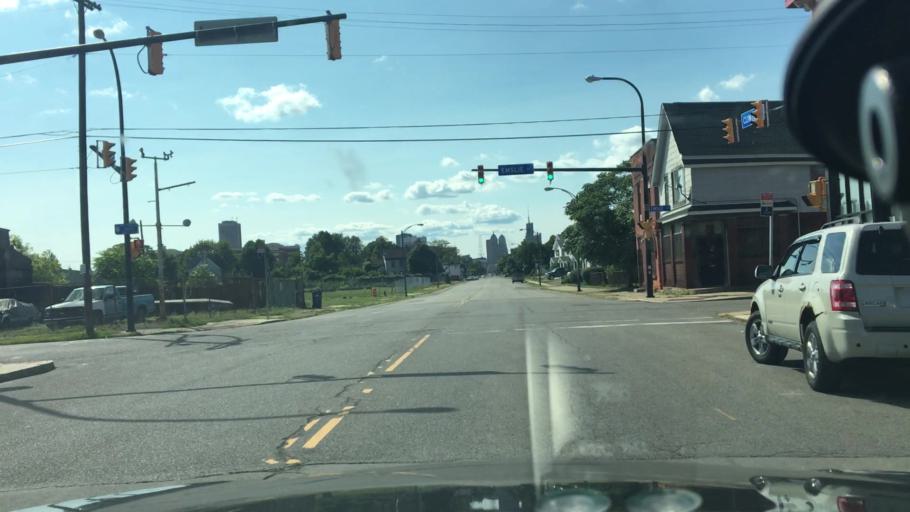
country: US
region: New York
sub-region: Erie County
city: Buffalo
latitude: 42.8810
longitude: -78.8487
